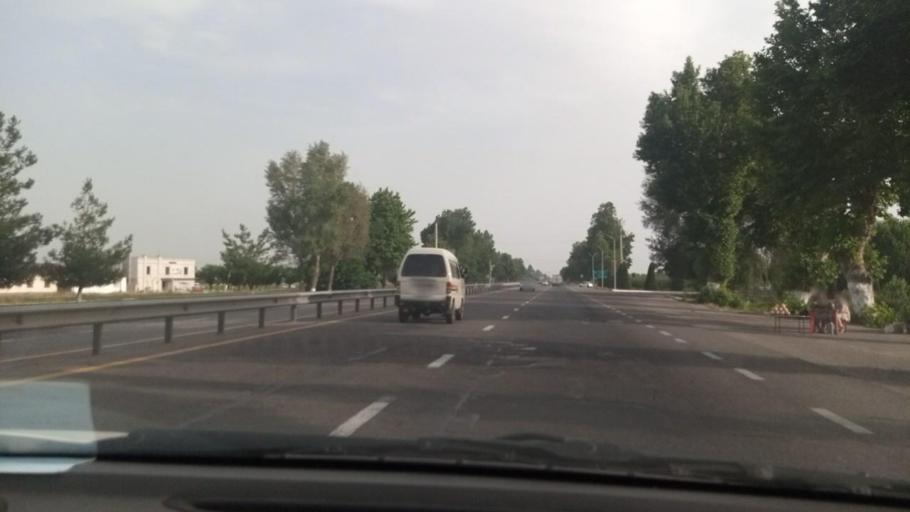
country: UZ
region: Toshkent Shahri
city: Bektemir
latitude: 41.2253
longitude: 69.4023
